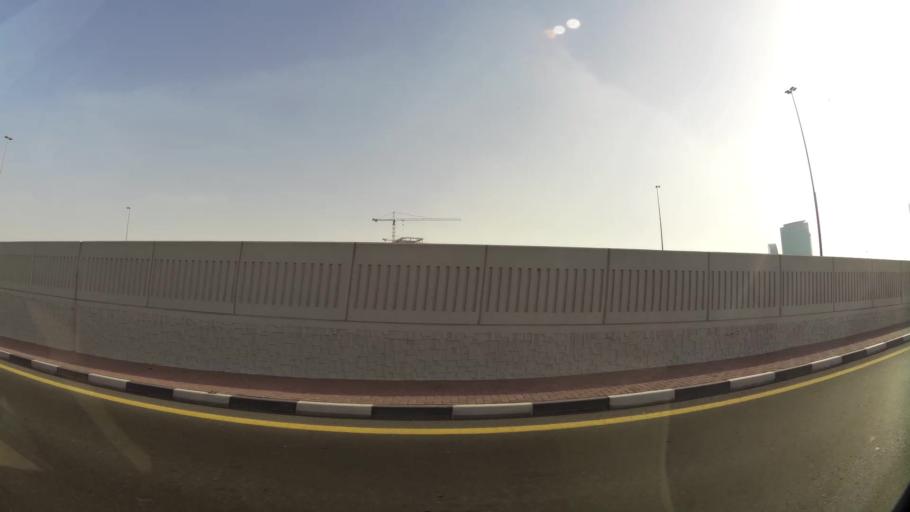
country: AE
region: Ash Shariqah
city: Sharjah
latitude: 25.2260
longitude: 55.3596
